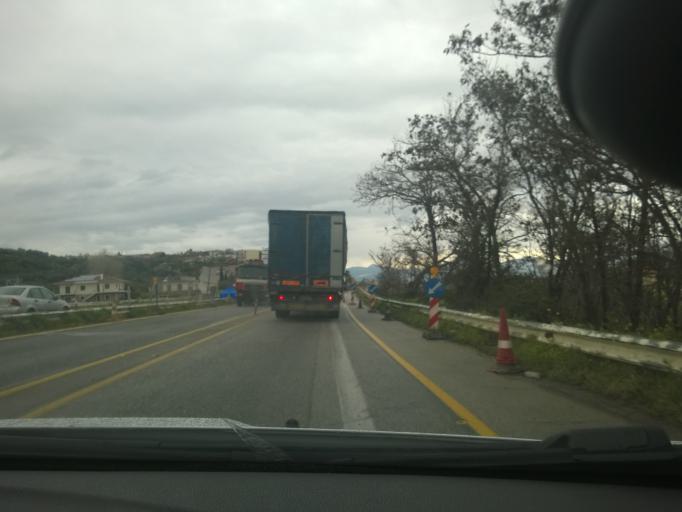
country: GR
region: West Greece
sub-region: Nomos Achaias
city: Siliveniotika
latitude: 38.1559
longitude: 22.3421
